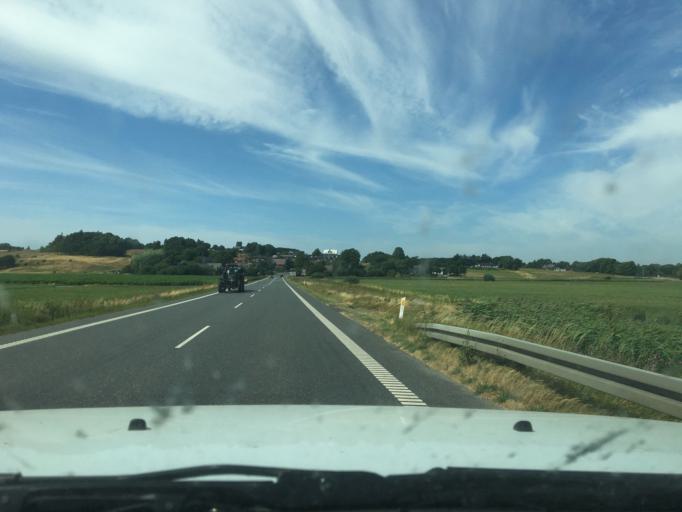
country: DK
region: Central Jutland
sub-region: Viborg Kommune
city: Viborg
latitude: 56.5718
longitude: 9.3809
